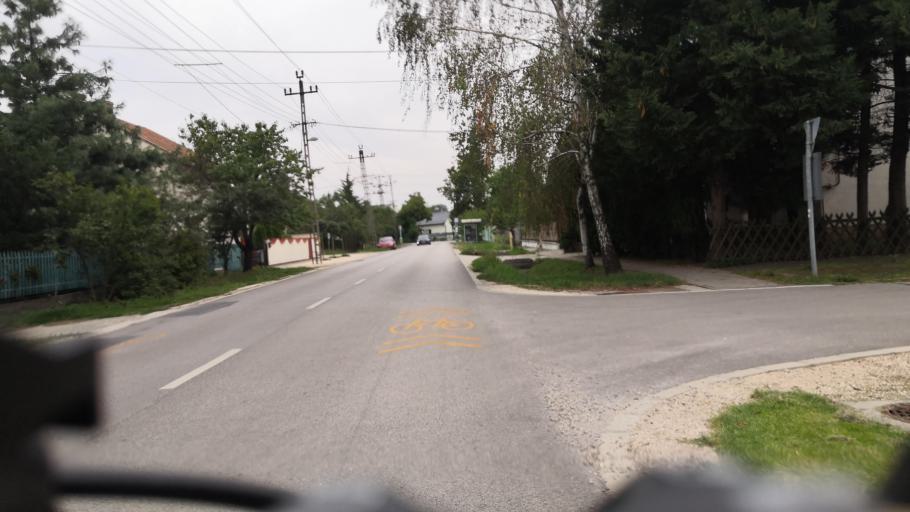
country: HU
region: Csongrad
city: Szeged
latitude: 46.2819
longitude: 20.1662
